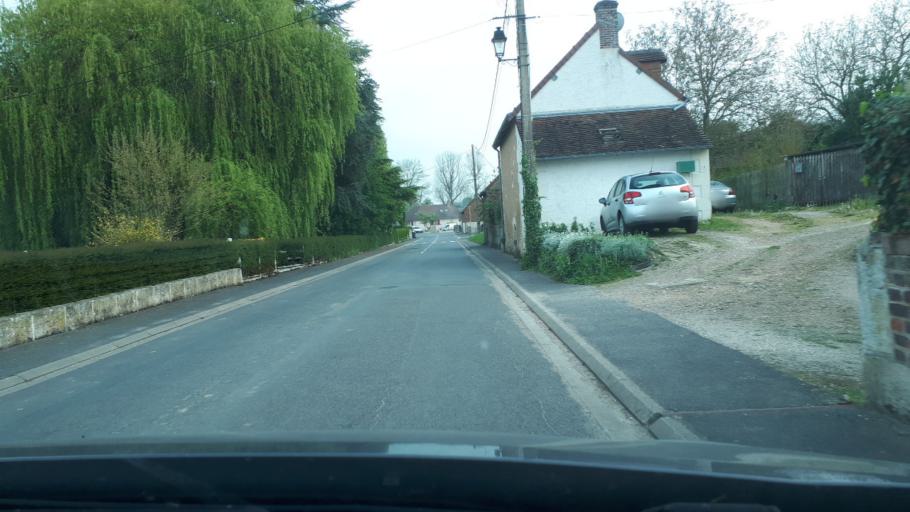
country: FR
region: Centre
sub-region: Departement du Loir-et-Cher
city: Lunay
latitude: 47.8221
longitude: 0.9474
